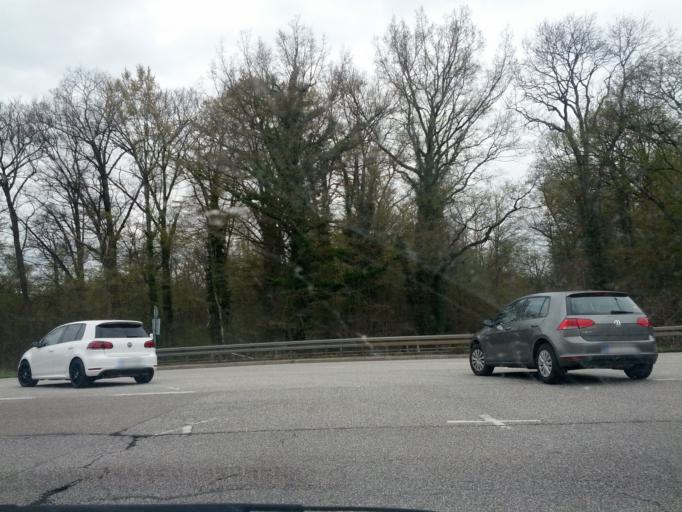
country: DE
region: Baden-Wuerttemberg
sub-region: Freiburg Region
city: Gundelfingen
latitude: 48.0318
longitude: 7.8418
